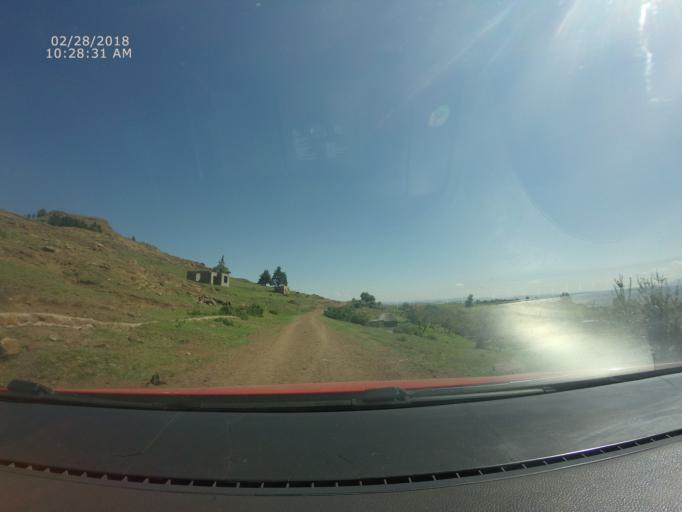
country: LS
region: Berea
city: Teyateyaneng
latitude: -29.2202
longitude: 27.8669
